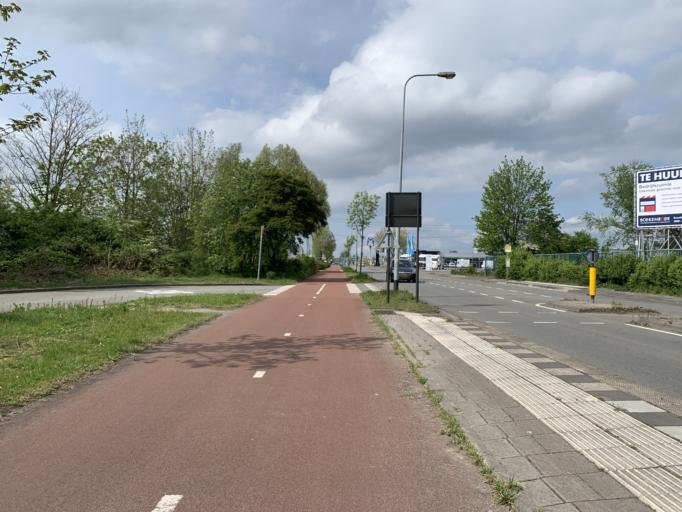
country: NL
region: Groningen
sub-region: Gemeente Groningen
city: Oosterpark
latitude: 53.2076
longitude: 6.5968
